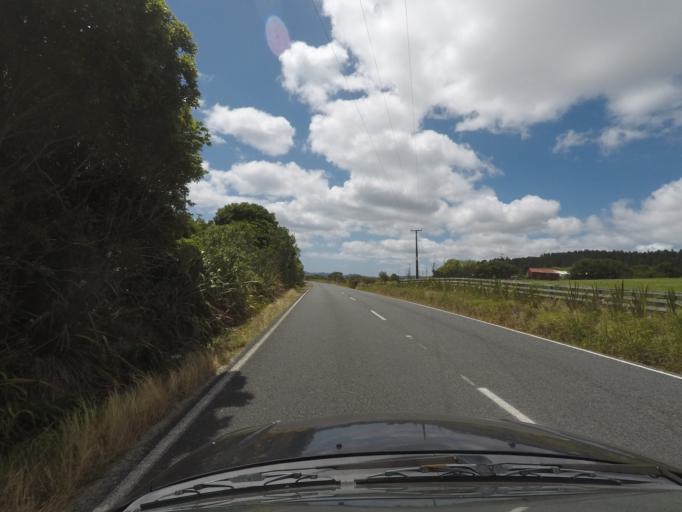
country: NZ
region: Northland
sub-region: Whangarei
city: Ruakaka
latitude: -36.0143
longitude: 174.4843
